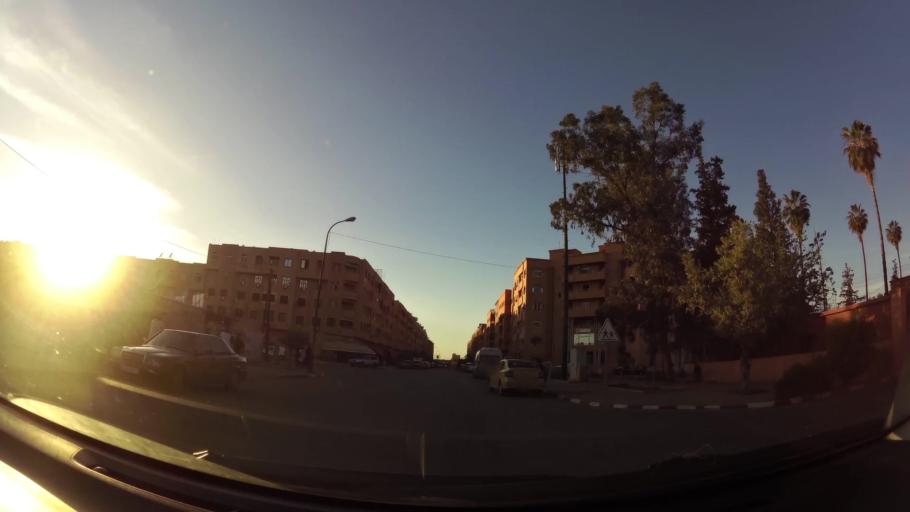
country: MA
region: Marrakech-Tensift-Al Haouz
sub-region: Marrakech
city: Marrakesh
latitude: 31.6203
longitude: -8.0269
